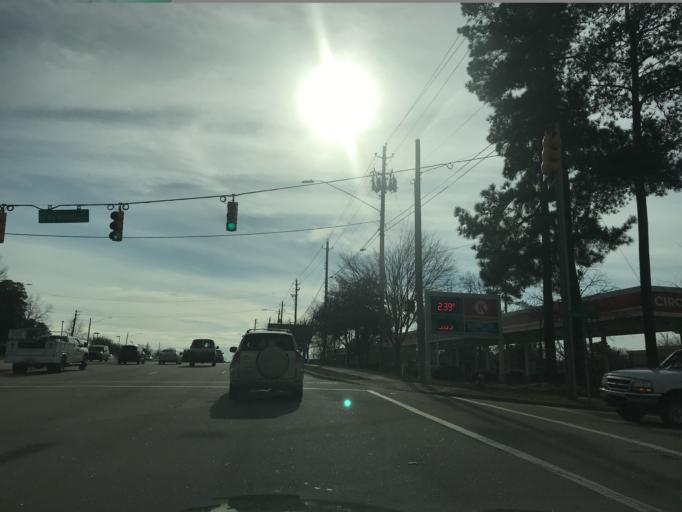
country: US
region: North Carolina
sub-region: Wake County
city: Raleigh
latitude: 35.8324
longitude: -78.5844
